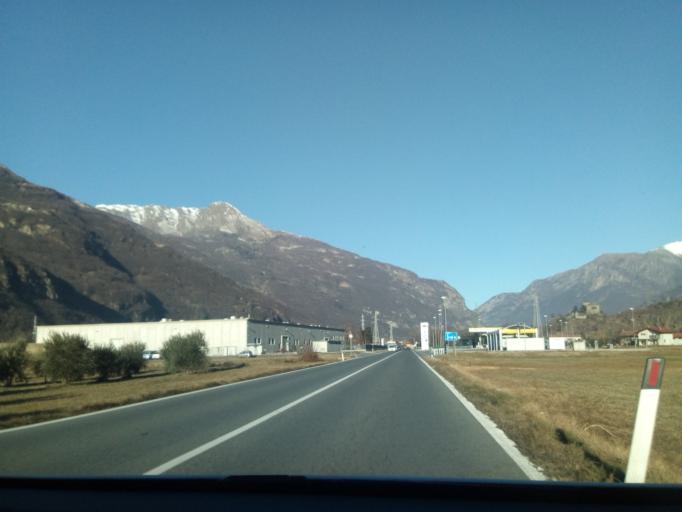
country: IT
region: Piedmont
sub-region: Provincia di Torino
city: Quassolo
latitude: 45.5320
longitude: 7.8446
